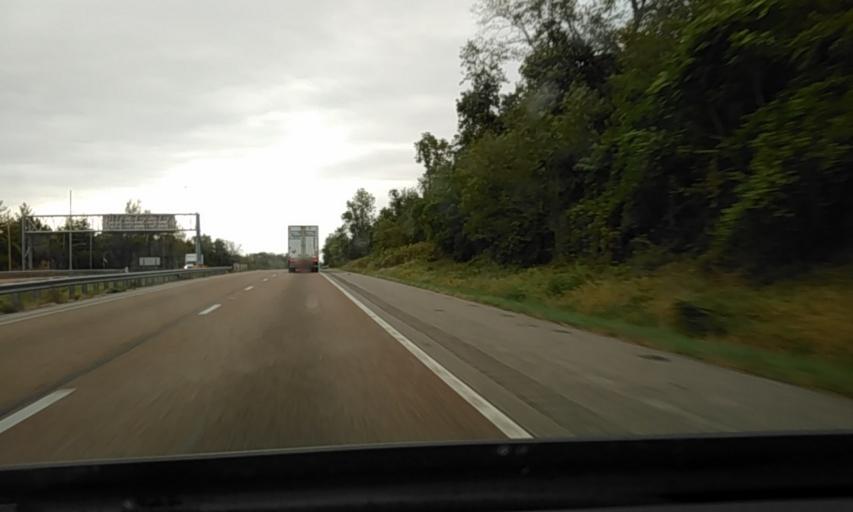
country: US
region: Illinois
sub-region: Madison County
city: Collinsville
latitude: 38.6939
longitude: -89.9978
